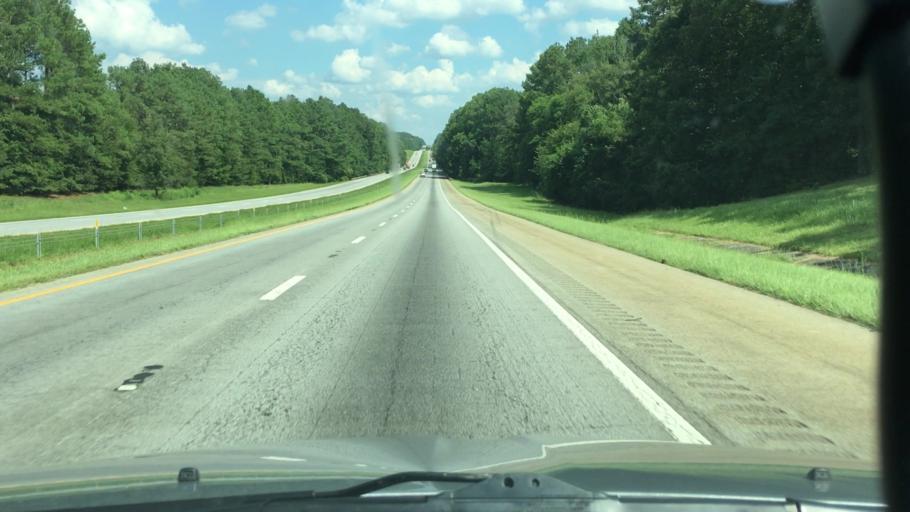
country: US
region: South Carolina
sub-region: Newberry County
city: Newberry
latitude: 34.3584
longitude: -81.6570
